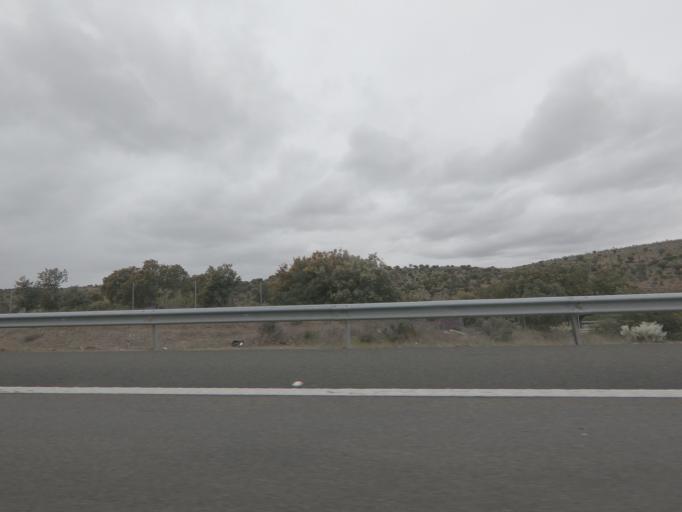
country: ES
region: Extremadura
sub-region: Provincia de Caceres
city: Mirabel
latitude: 39.9068
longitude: -6.2536
